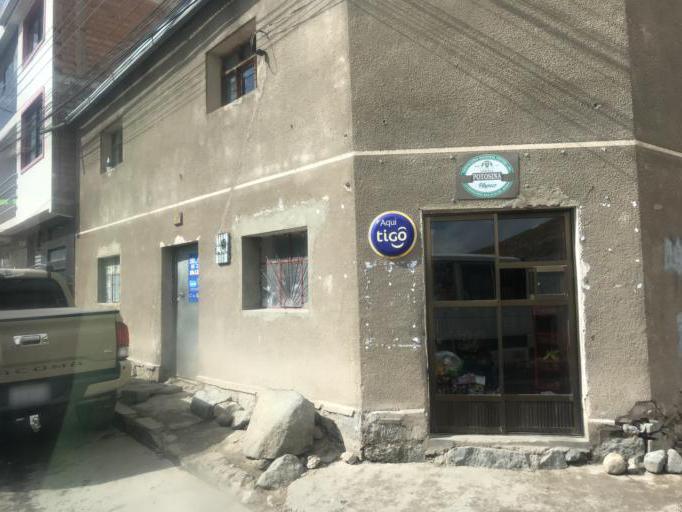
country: BO
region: Potosi
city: Potosi
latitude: -19.6009
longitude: -65.7445
